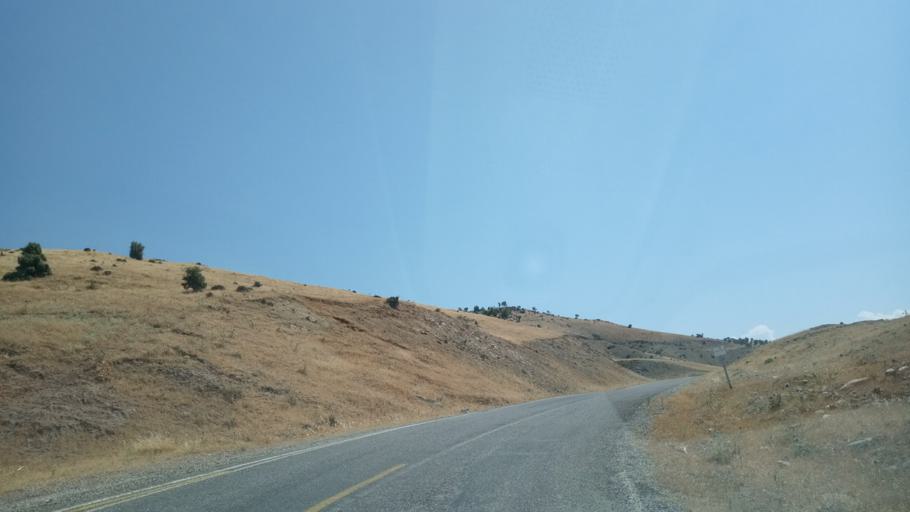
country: TR
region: Siirt
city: Dilektepe
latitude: 38.0688
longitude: 41.8271
